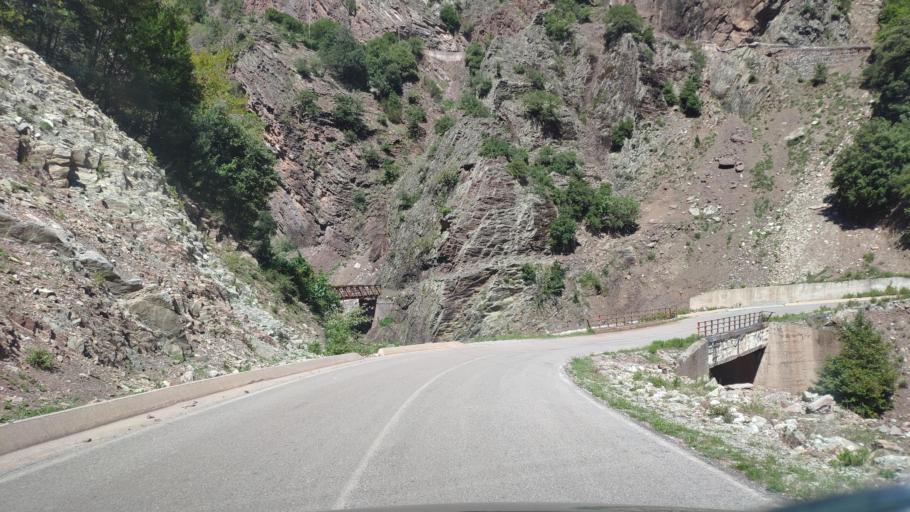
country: GR
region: Central Greece
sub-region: Nomos Evrytanias
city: Kerasochori
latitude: 39.0799
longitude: 21.5954
